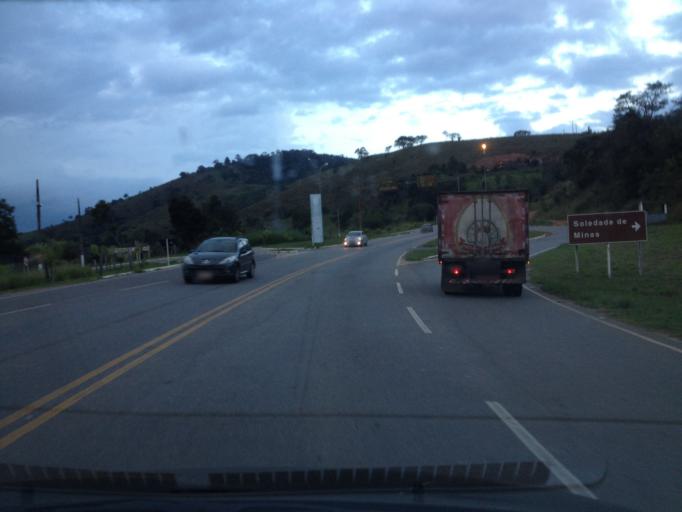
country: BR
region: Minas Gerais
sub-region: Sao Lourenco
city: Sao Lourenco
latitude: -22.0579
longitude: -45.0381
